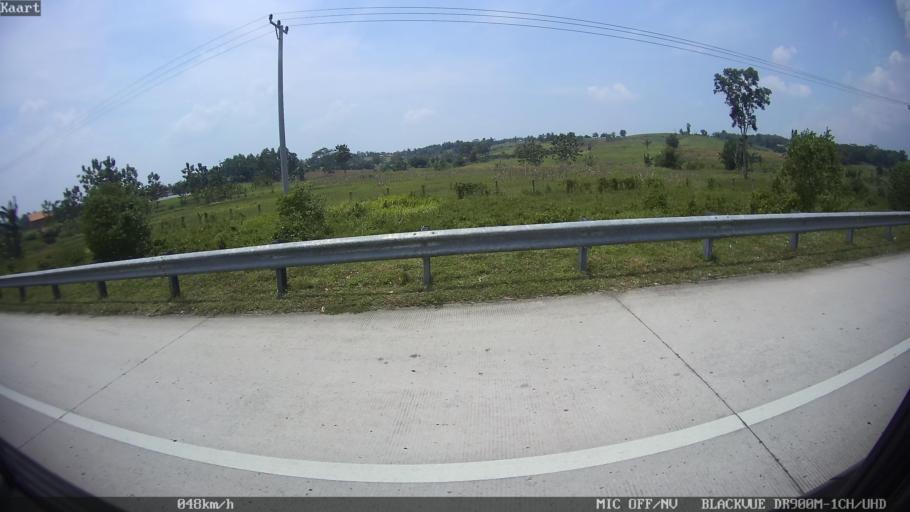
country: ID
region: Lampung
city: Natar
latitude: -5.2797
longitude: 105.2076
